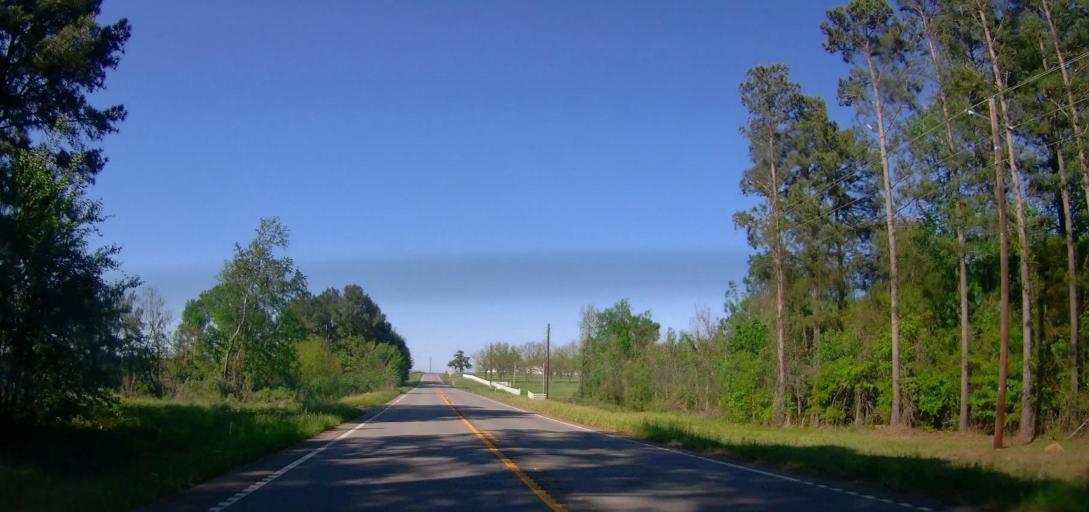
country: US
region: Georgia
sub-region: Pulaski County
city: Hawkinsville
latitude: 32.1699
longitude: -83.5112
